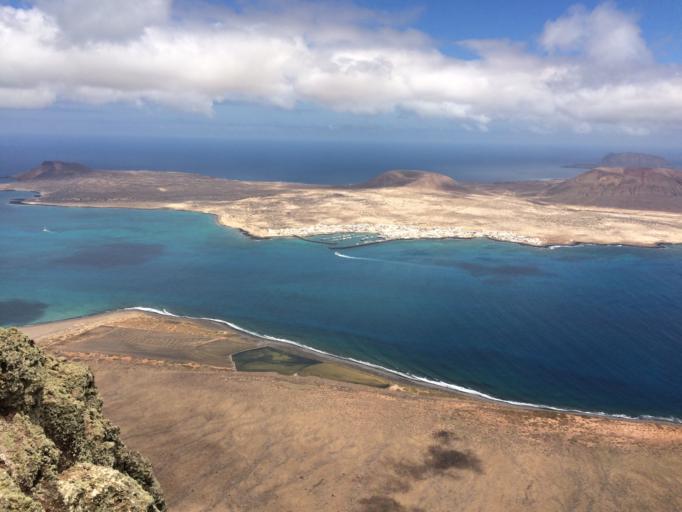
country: ES
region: Canary Islands
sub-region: Provincia de Las Palmas
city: Haria
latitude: 29.2145
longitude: -13.4814
